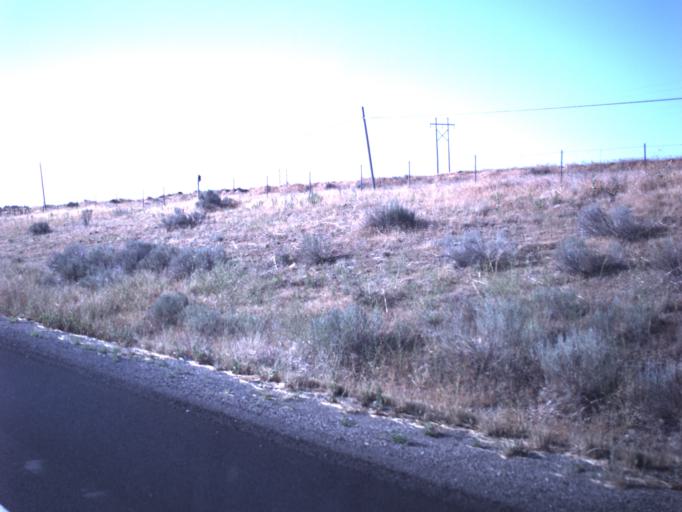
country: US
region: Utah
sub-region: Salt Lake County
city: Magna
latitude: 40.6605
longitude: -112.0853
